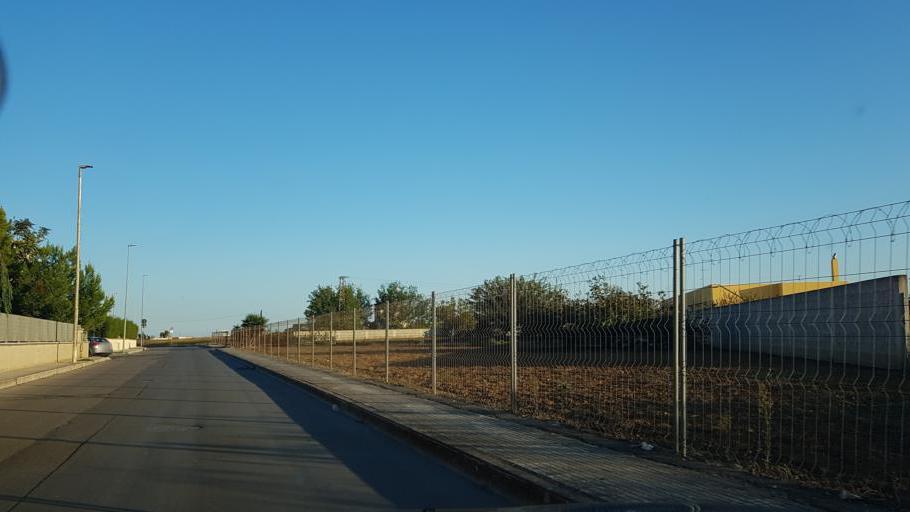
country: IT
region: Apulia
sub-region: Provincia di Brindisi
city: Brindisi
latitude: 40.6174
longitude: 17.9167
